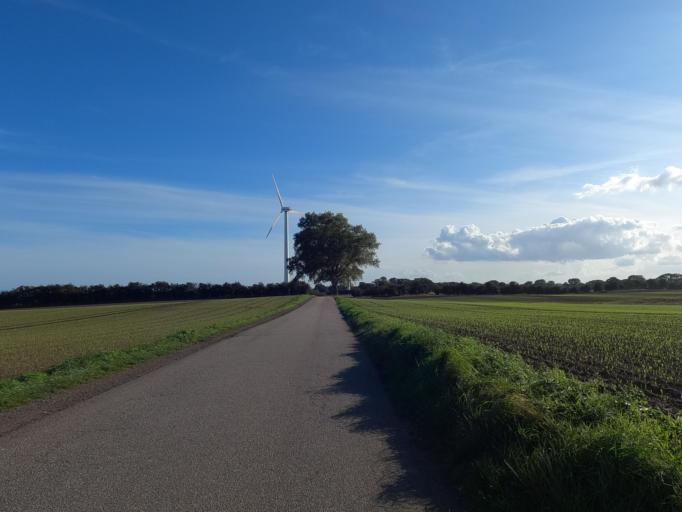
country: DE
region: Schleswig-Holstein
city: Neukirchen
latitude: 54.3414
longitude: 11.0505
